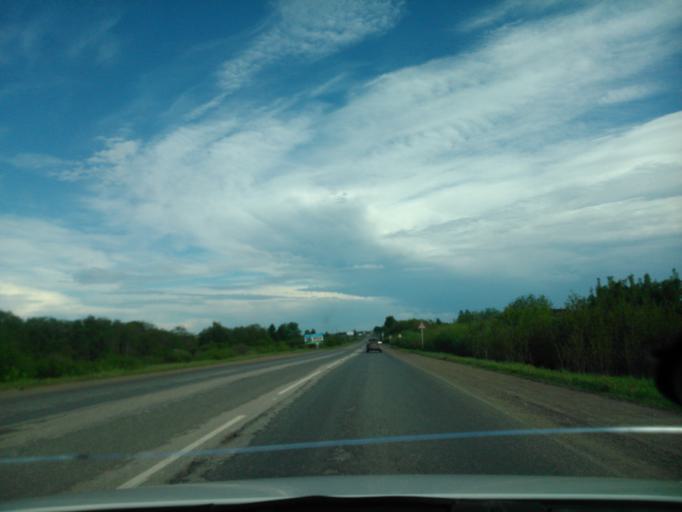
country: RU
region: Perm
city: Lobanovo
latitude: 57.8762
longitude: 56.2744
